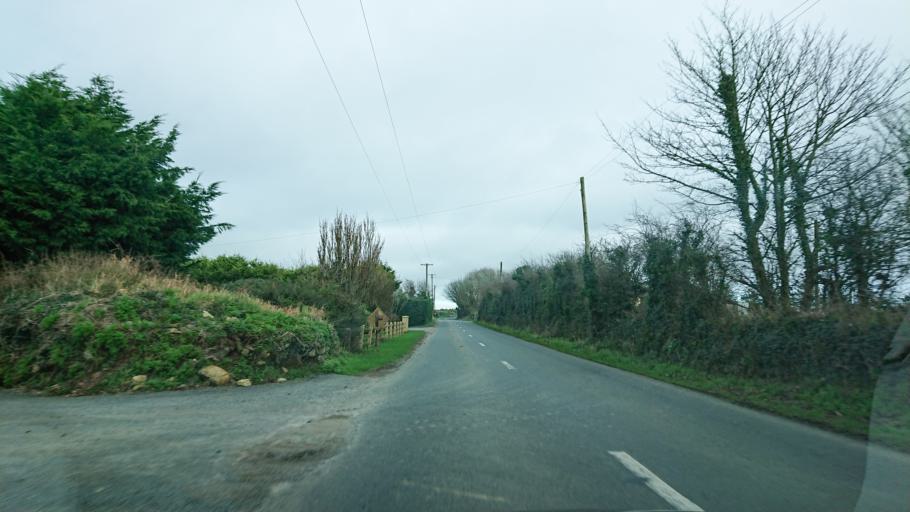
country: IE
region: Leinster
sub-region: Kilkenny
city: Mooncoin
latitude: 52.1921
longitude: -7.2788
